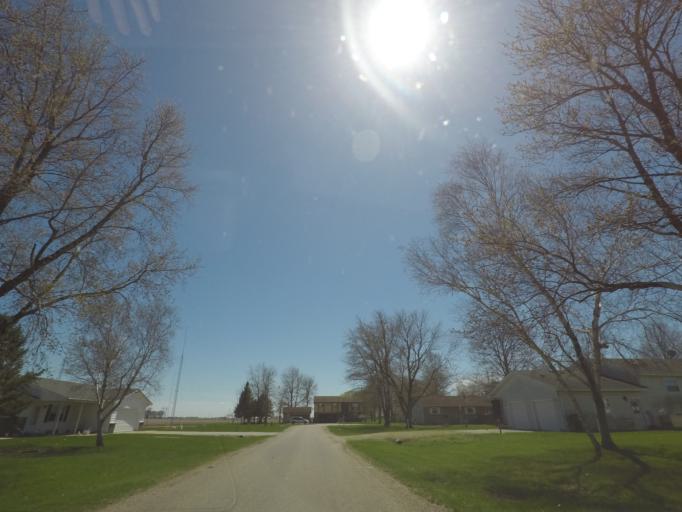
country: US
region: Illinois
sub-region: Macon County
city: Warrensburg
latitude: 39.9673
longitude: -89.1568
